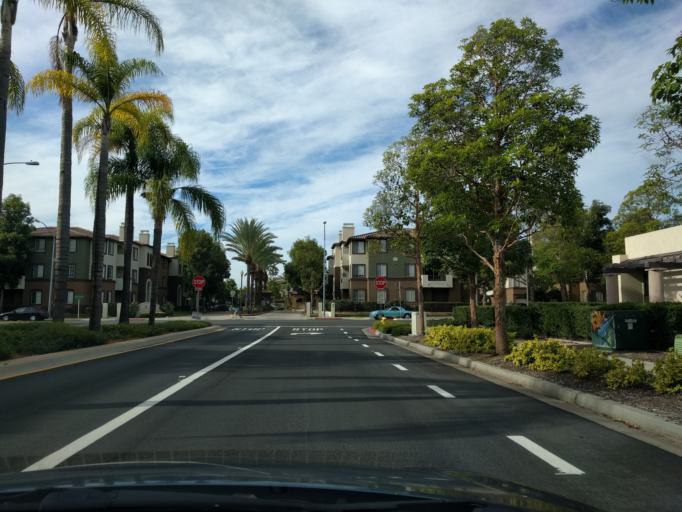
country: US
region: California
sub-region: San Diego County
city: San Diego
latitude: 32.7743
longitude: -117.1463
